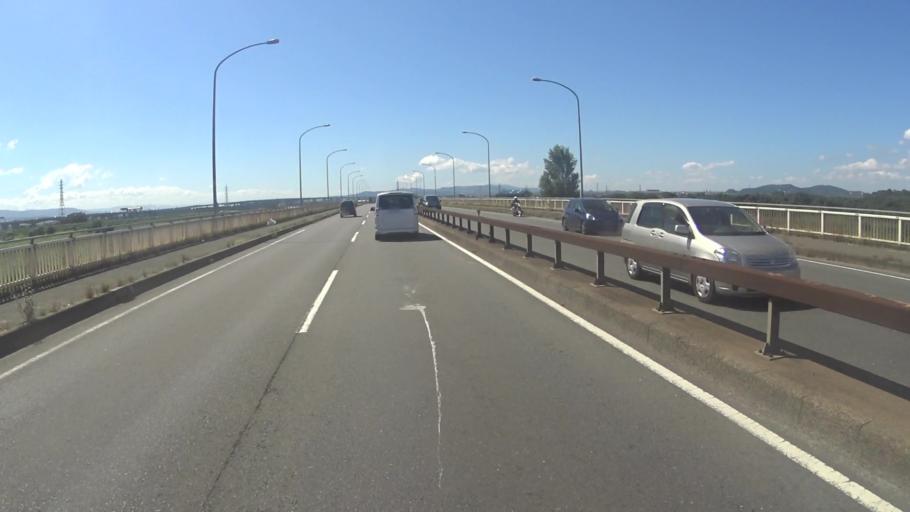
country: JP
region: Kyoto
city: Yawata
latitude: 34.9171
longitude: 135.7447
